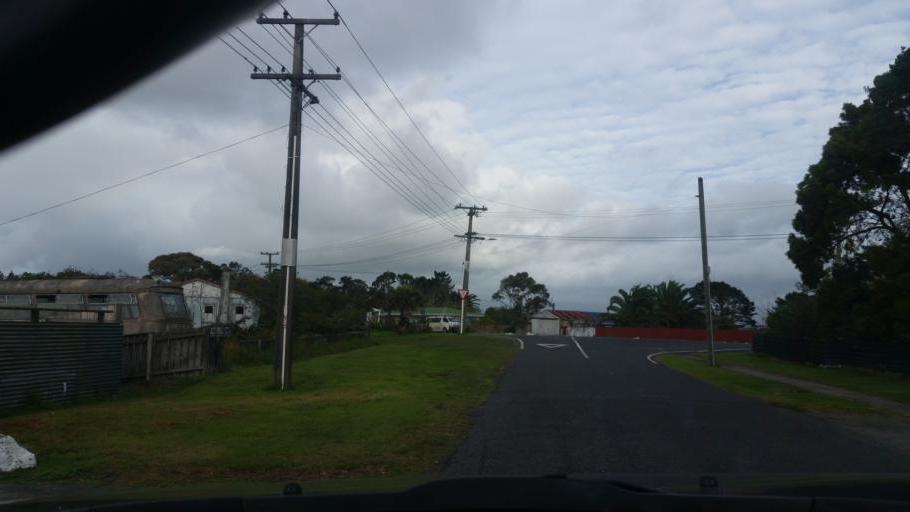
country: NZ
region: Northland
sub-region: Kaipara District
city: Dargaville
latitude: -36.0314
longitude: 173.9178
